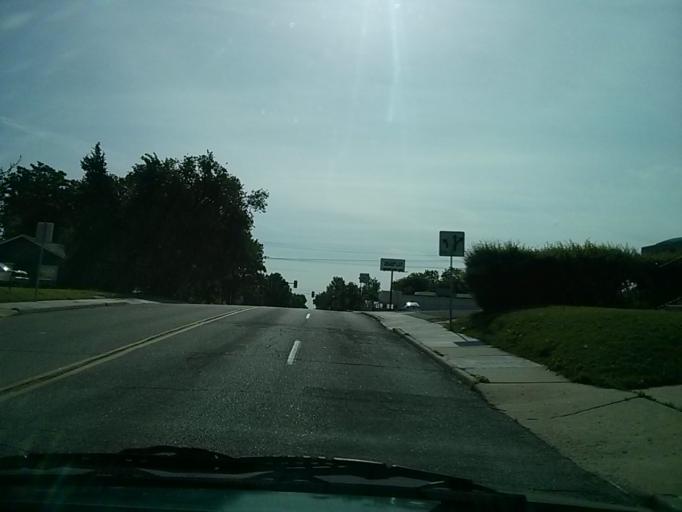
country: US
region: Oklahoma
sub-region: Tulsa County
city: Tulsa
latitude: 36.1550
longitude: -95.9239
